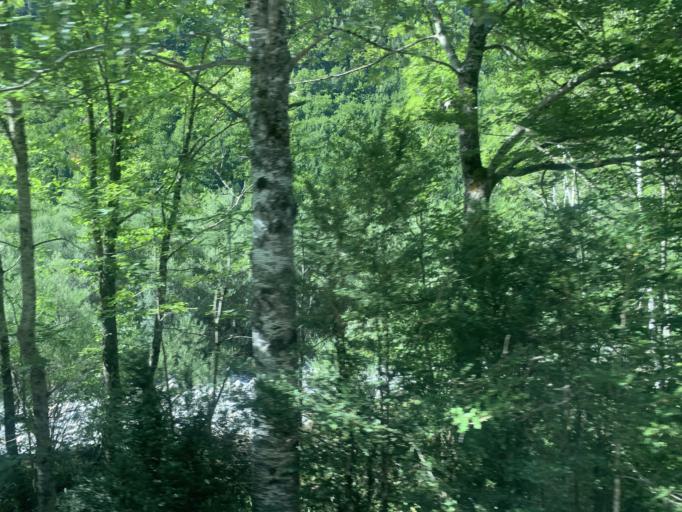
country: ES
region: Aragon
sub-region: Provincia de Huesca
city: Broto
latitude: 42.6492
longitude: -0.0632
